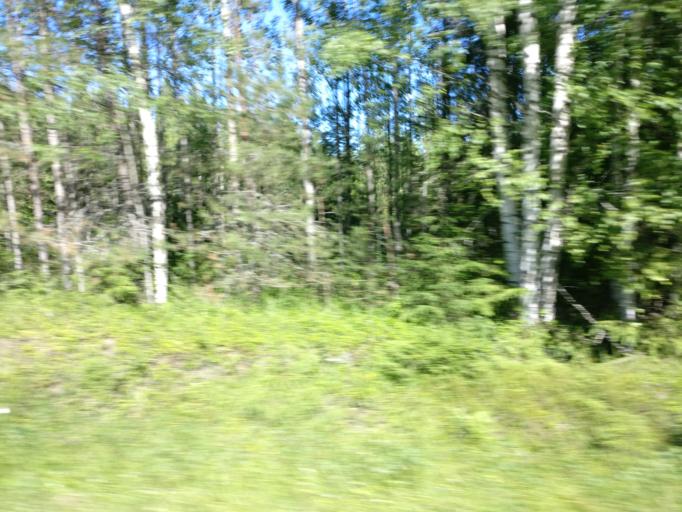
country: FI
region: Southern Savonia
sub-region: Savonlinna
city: Rantasalmi
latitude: 62.0958
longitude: 28.2740
